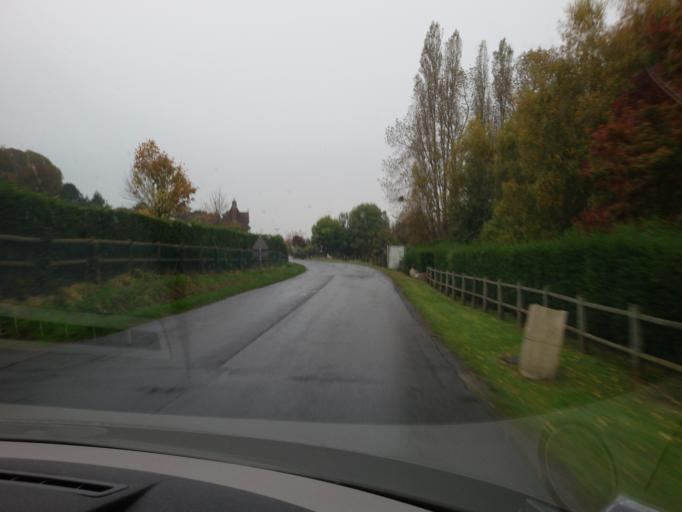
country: FR
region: Lower Normandy
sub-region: Departement du Calvados
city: Equemauville
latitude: 49.4021
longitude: 0.1418
